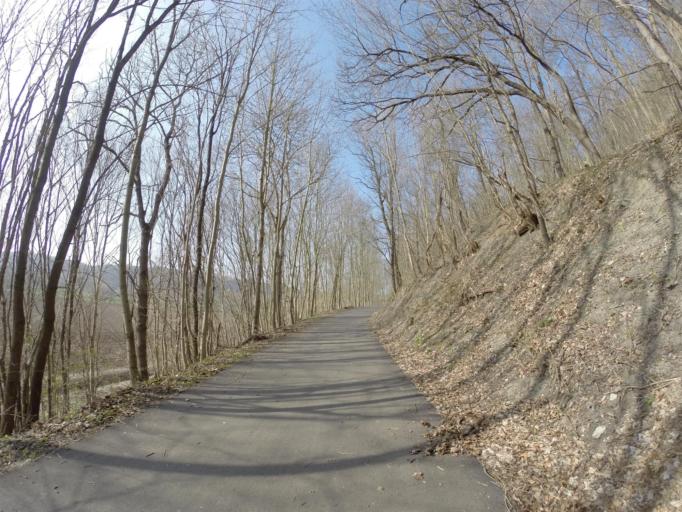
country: DE
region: Thuringia
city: Golmsdorf
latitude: 50.9895
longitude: 11.6753
